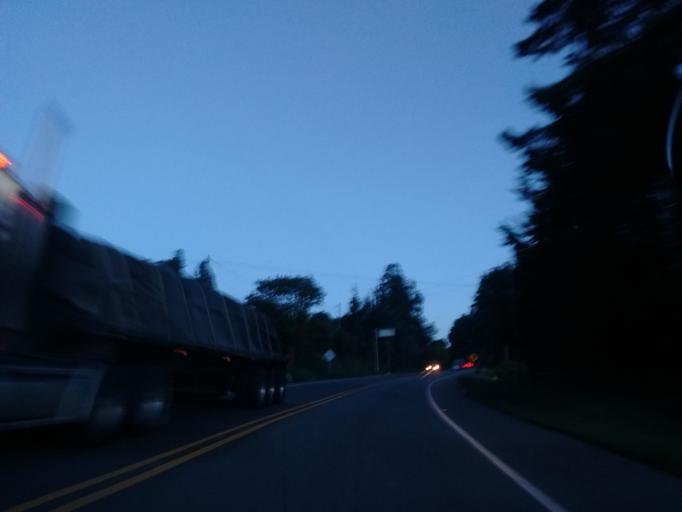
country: CO
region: Antioquia
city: Santuario
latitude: 6.1223
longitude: -75.2363
